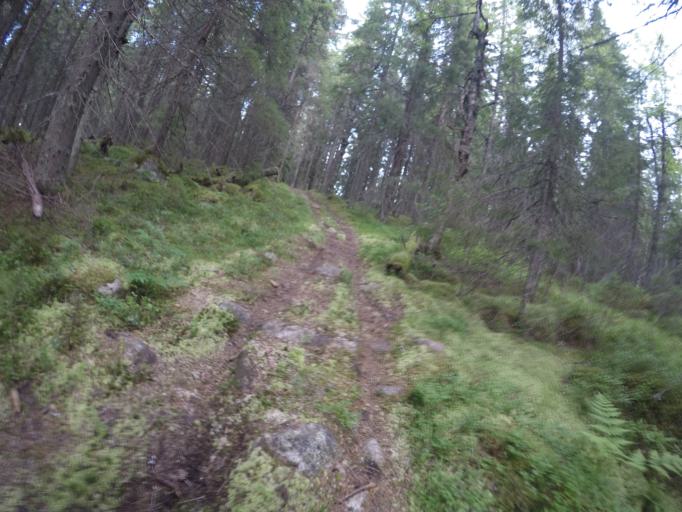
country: SE
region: Vaermland
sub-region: Filipstads Kommun
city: Lesjofors
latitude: 60.2038
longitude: 14.2897
